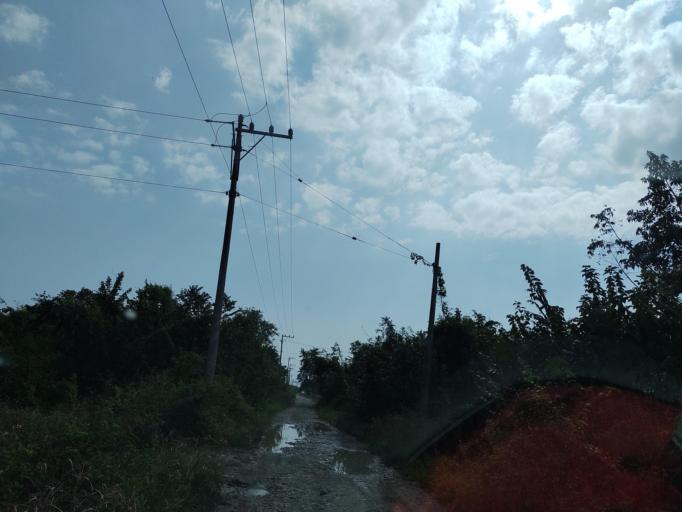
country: MX
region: Puebla
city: Espinal
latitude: 20.2798
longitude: -97.3348
